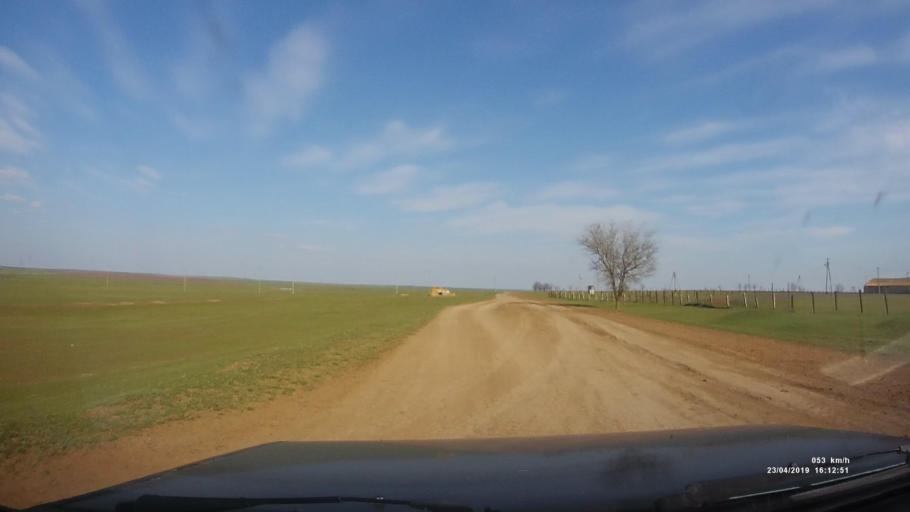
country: RU
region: Kalmykiya
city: Priyutnoye
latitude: 46.4649
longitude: 43.1306
